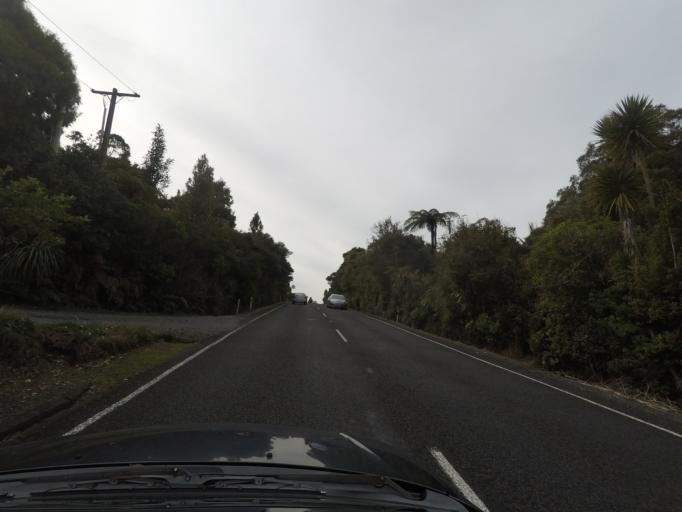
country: NZ
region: Auckland
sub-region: Auckland
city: Titirangi
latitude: -36.9470
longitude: 174.5247
